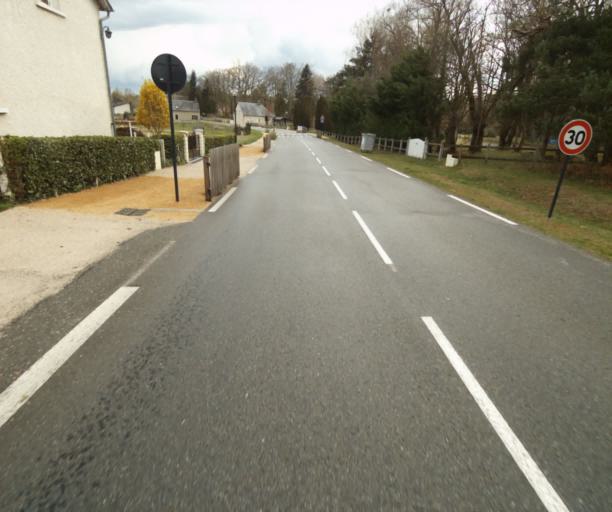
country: FR
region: Limousin
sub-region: Departement de la Correze
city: Saint-Privat
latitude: 45.2250
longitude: 2.0060
